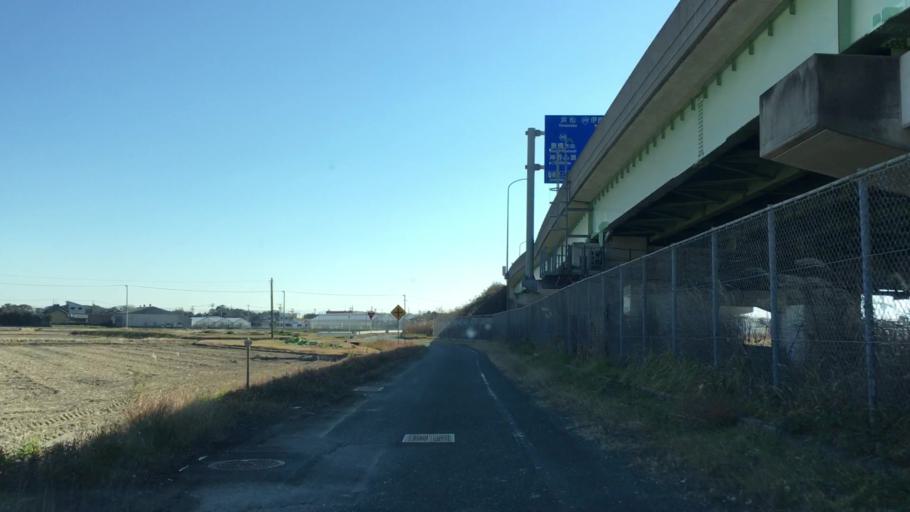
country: JP
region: Aichi
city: Toyohashi
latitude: 34.7310
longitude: 137.3530
